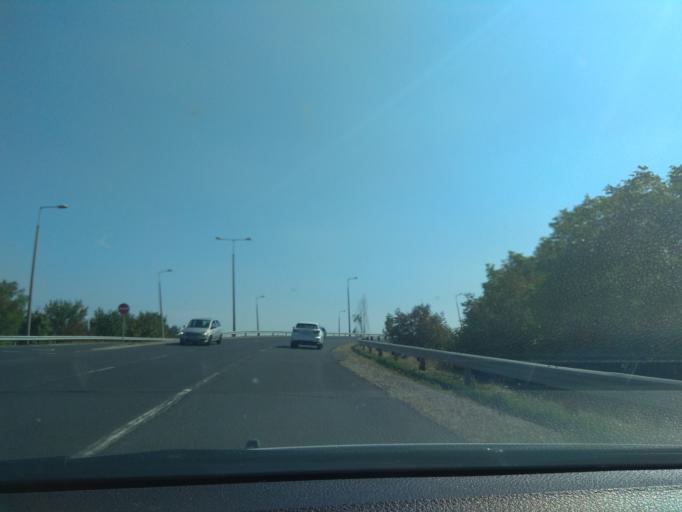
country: HU
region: Borsod-Abauj-Zemplen
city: Miskolc
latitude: 48.0538
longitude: 20.7996
